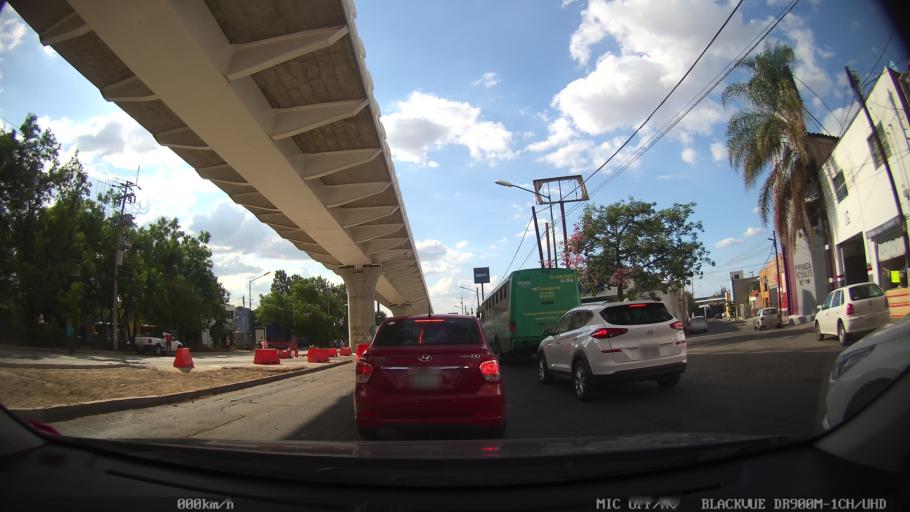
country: MX
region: Jalisco
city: Tlaquepaque
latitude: 20.6397
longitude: -103.3012
